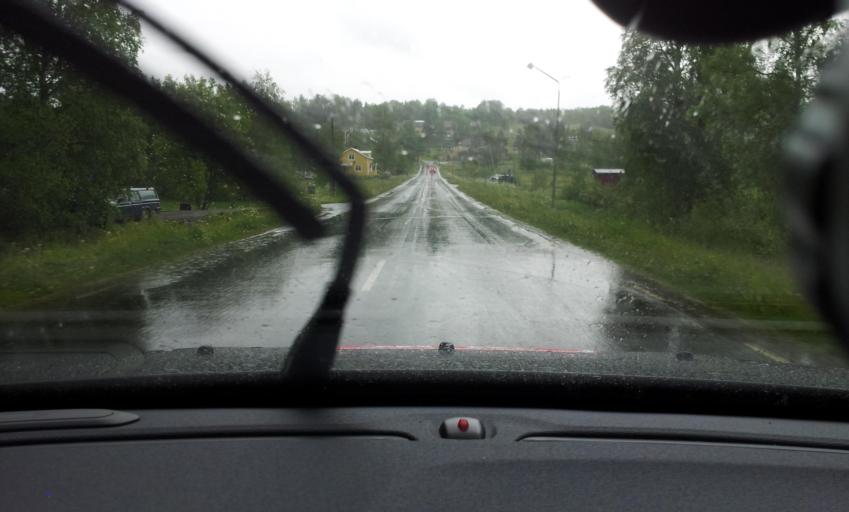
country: SE
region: Jaemtland
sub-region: Are Kommun
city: Are
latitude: 63.3130
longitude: 13.2326
